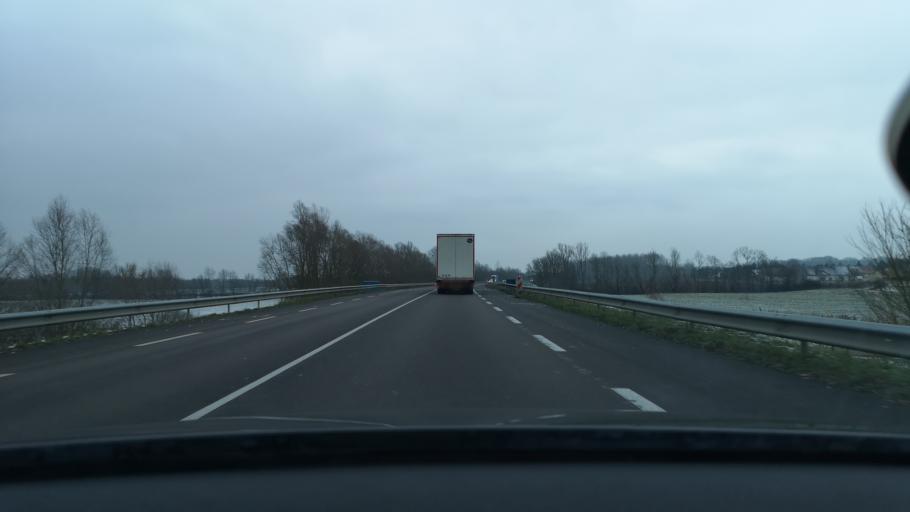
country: FR
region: Bourgogne
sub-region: Departement de Saone-et-Loire
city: Saint-Marcel
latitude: 46.7837
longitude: 4.8881
